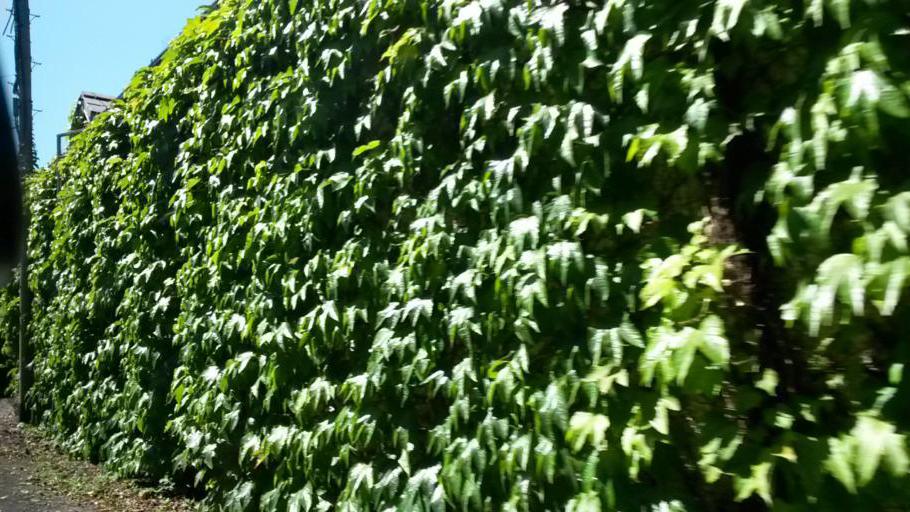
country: IE
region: Leinster
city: Ballymun
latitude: 53.4542
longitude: -6.2781
